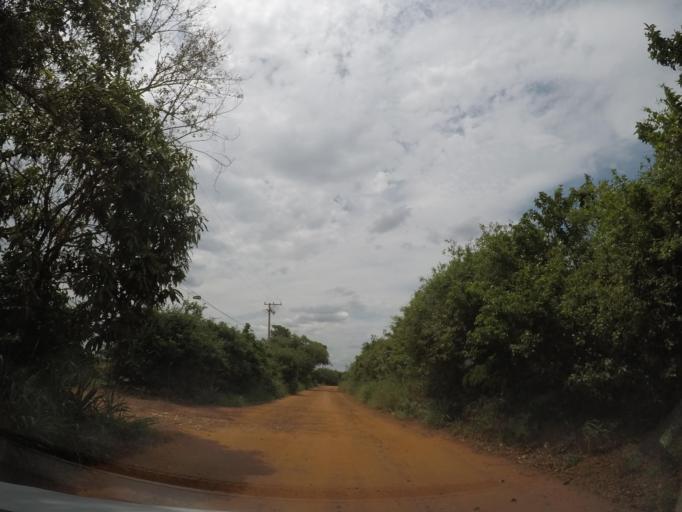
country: BR
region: Sao Paulo
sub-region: Sumare
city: Sumare
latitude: -22.8456
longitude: -47.2933
